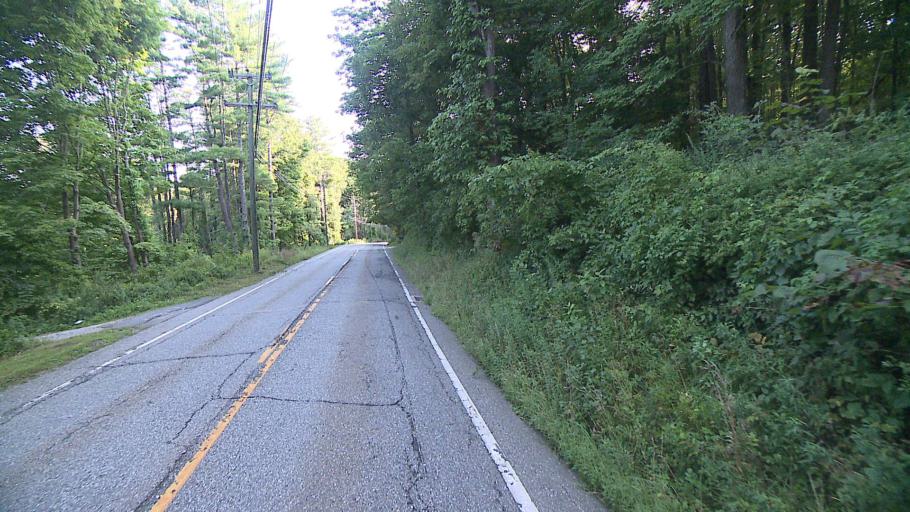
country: US
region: Connecticut
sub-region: Litchfield County
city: Kent
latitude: 41.8118
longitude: -73.3761
